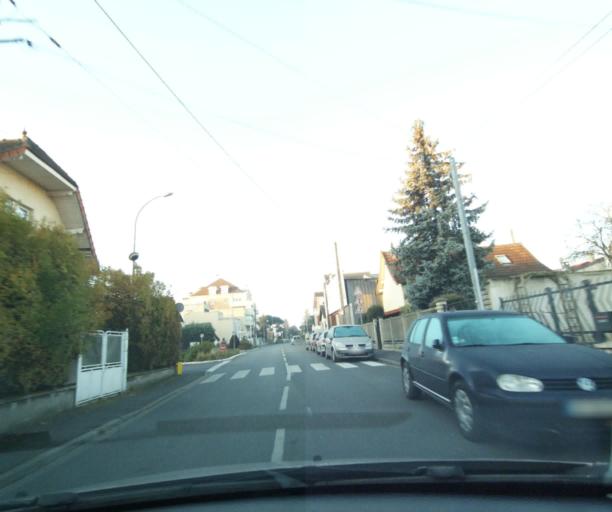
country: FR
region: Ile-de-France
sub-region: Departement de Seine-Saint-Denis
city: Gagny
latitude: 48.8717
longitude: 2.5349
